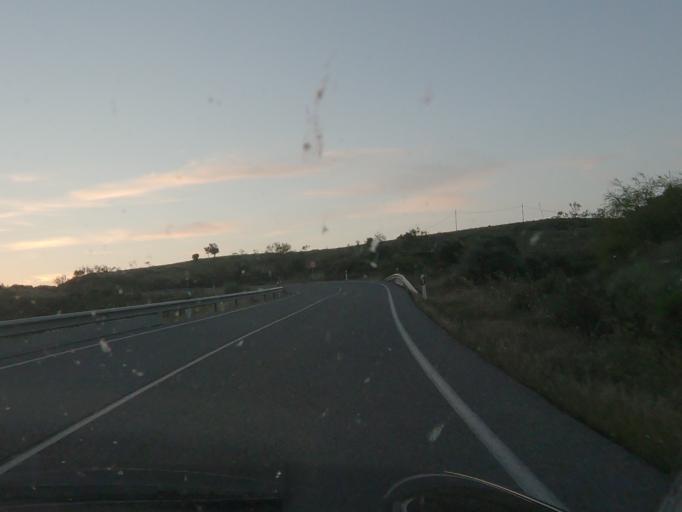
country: ES
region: Extremadura
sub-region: Provincia de Caceres
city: Alcantara
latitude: 39.7337
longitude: -6.9055
